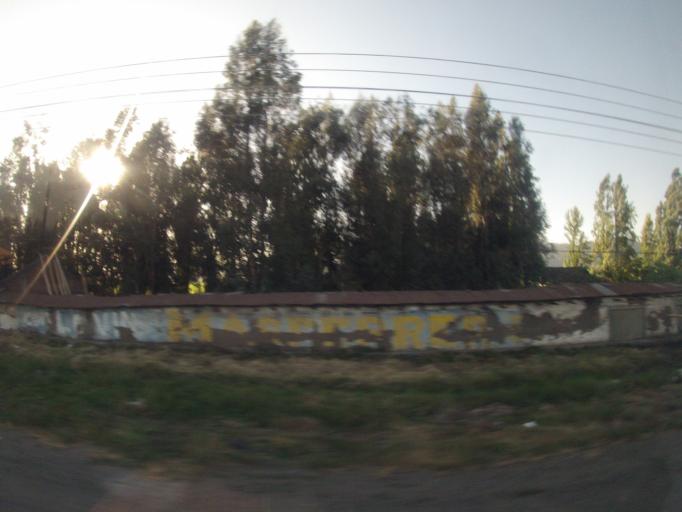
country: CL
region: O'Higgins
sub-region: Provincia de Colchagua
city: Chimbarongo
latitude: -34.7213
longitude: -71.0337
